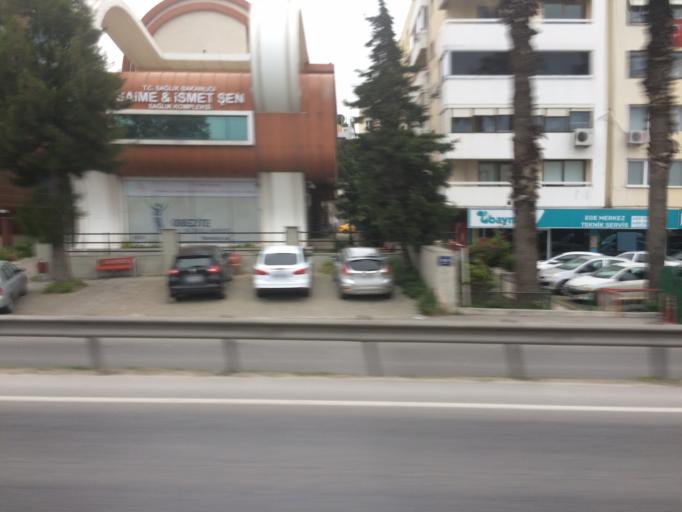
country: TR
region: Izmir
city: Karsiyaka
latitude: 38.4643
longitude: 27.1627
